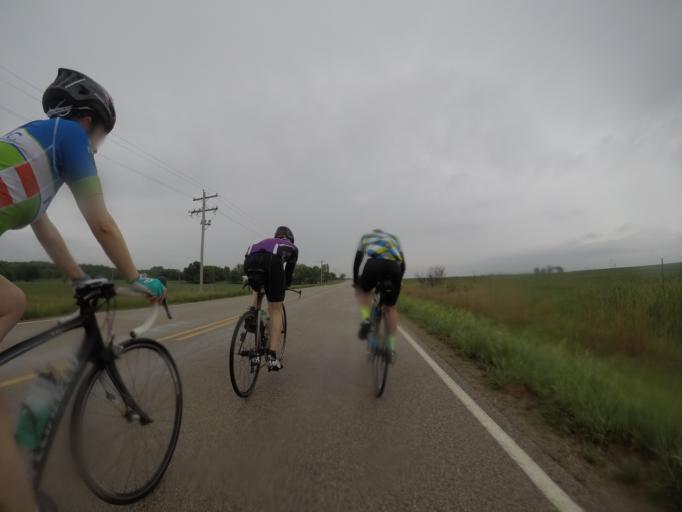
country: US
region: Kansas
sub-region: Pottawatomie County
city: Wamego
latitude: 39.3519
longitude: -96.2212
